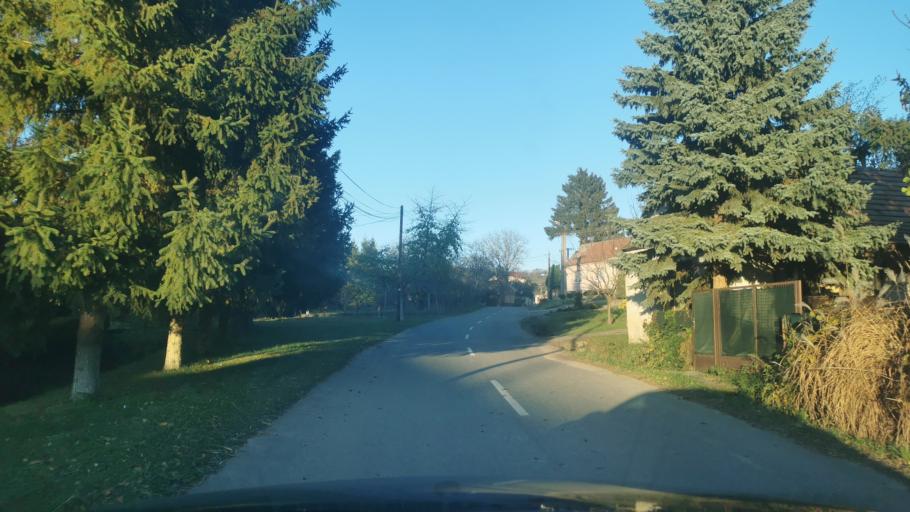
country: SK
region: Trnavsky
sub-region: Okres Senica
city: Senica
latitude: 48.7749
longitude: 17.3191
